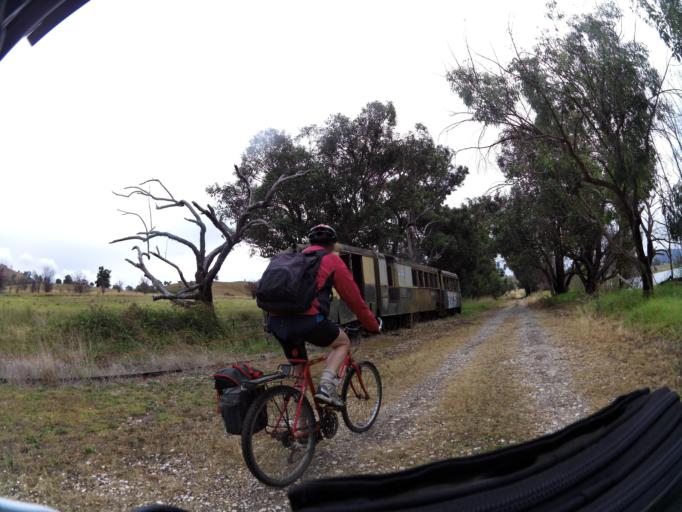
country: AU
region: New South Wales
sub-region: Albury Municipality
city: East Albury
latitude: -36.2186
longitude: 147.0648
